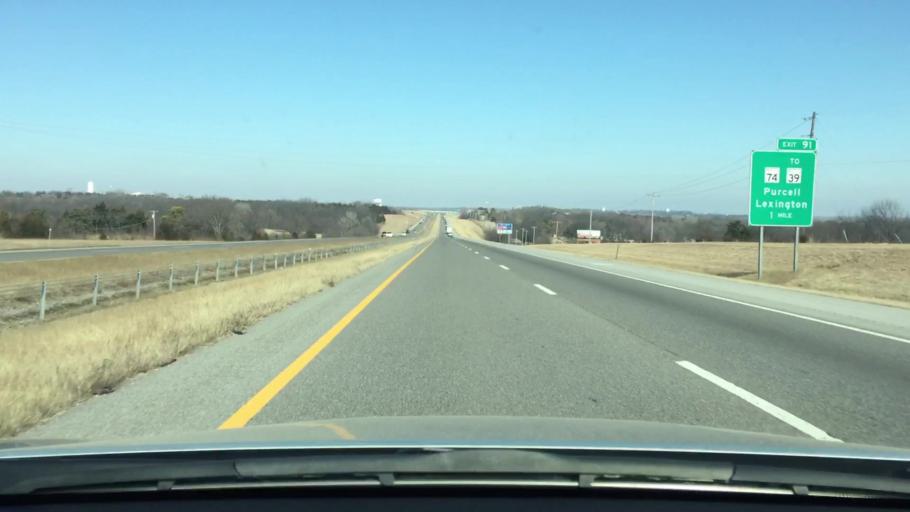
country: US
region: Oklahoma
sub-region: McClain County
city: Purcell
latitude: 34.9653
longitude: -97.3724
